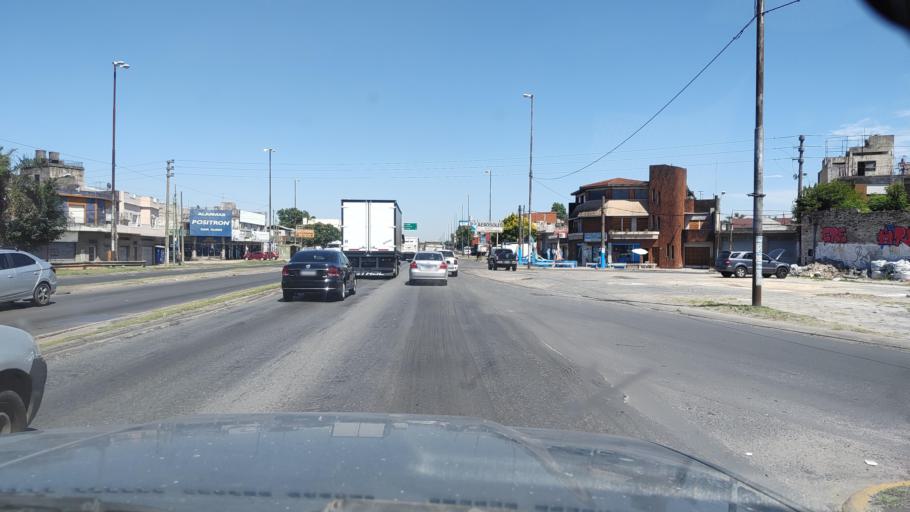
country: AR
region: Buenos Aires
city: San Justo
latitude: -34.6824
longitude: -58.5721
